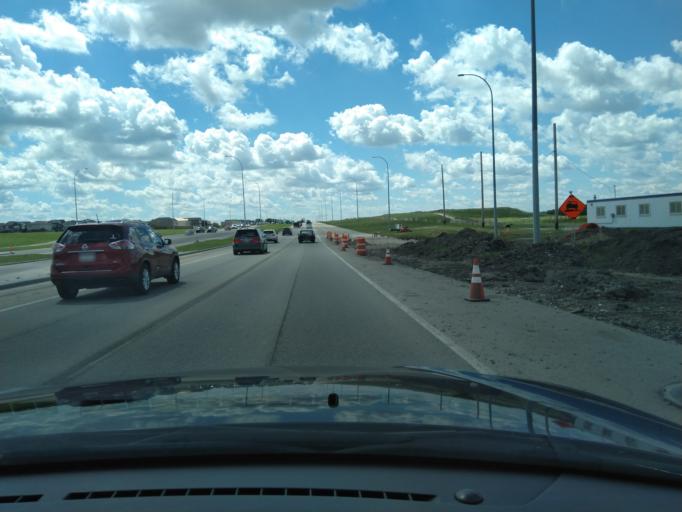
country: CA
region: Alberta
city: Calgary
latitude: 51.1394
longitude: -113.9703
